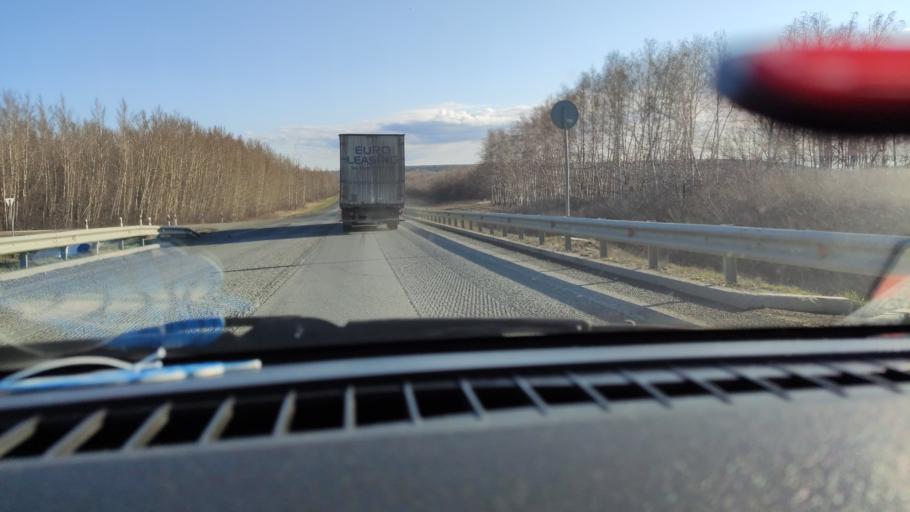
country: RU
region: Saratov
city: Dukhovnitskoye
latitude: 52.6914
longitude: 48.2443
